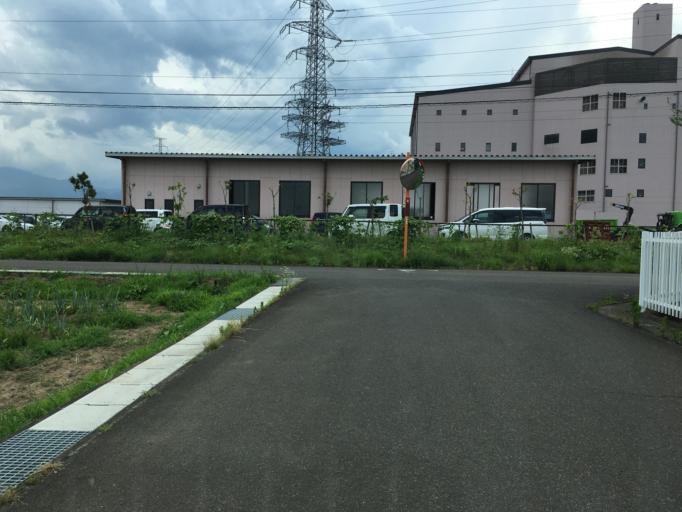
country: JP
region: Fukushima
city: Fukushima-shi
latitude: 37.7519
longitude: 140.4271
